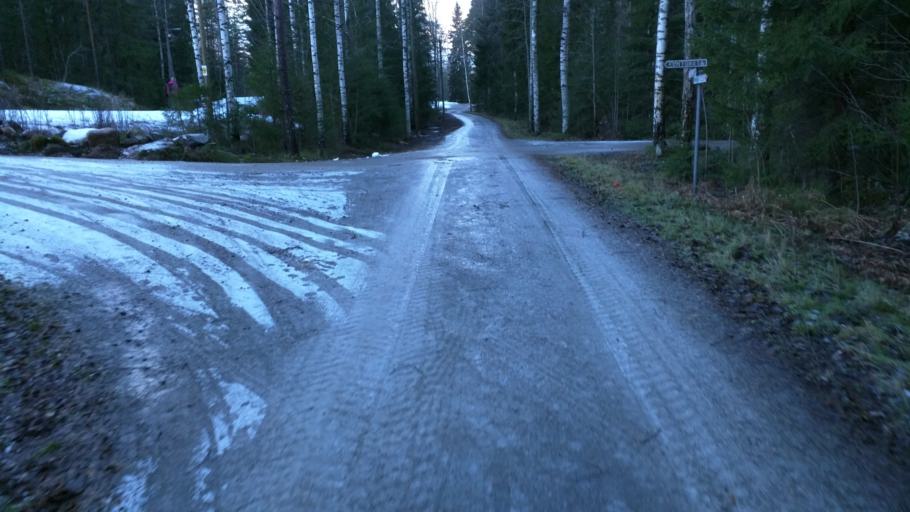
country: FI
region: Uusimaa
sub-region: Helsinki
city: Espoo
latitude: 60.2402
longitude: 24.6718
